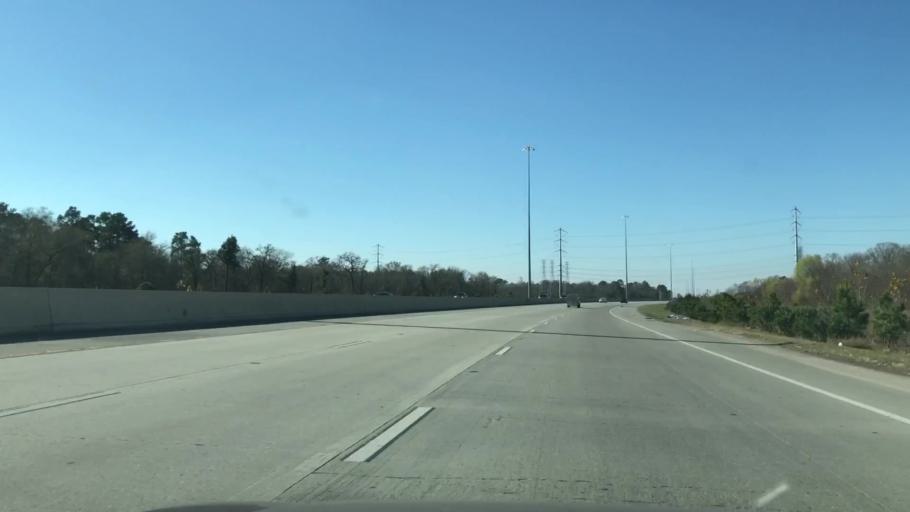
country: US
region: Texas
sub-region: Harris County
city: Jacinto City
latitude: 29.7966
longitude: -95.2266
